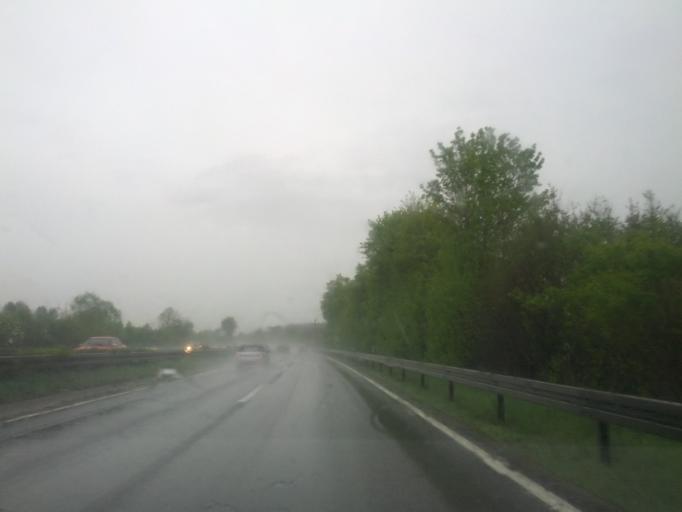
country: DE
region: Hesse
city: Allendorf an der Lahn
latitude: 50.5645
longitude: 8.6046
